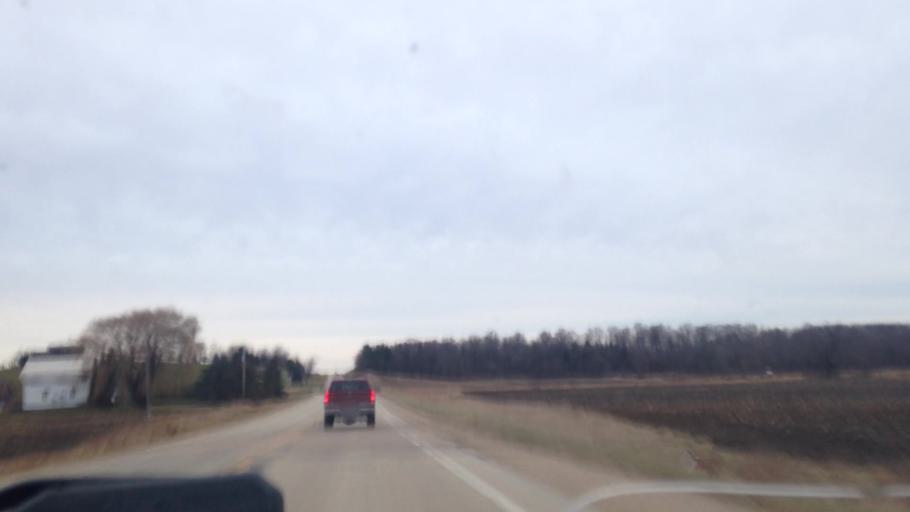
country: US
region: Wisconsin
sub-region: Dodge County
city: Theresa
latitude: 43.4577
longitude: -88.4503
